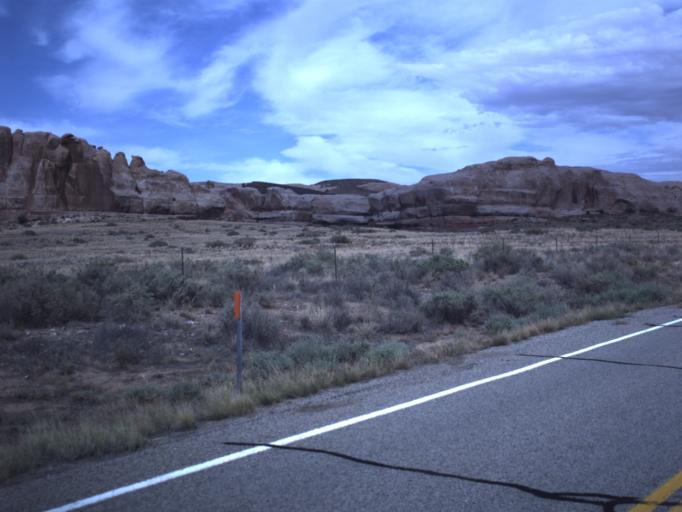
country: US
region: Utah
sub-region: San Juan County
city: Blanding
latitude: 37.2824
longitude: -109.5062
